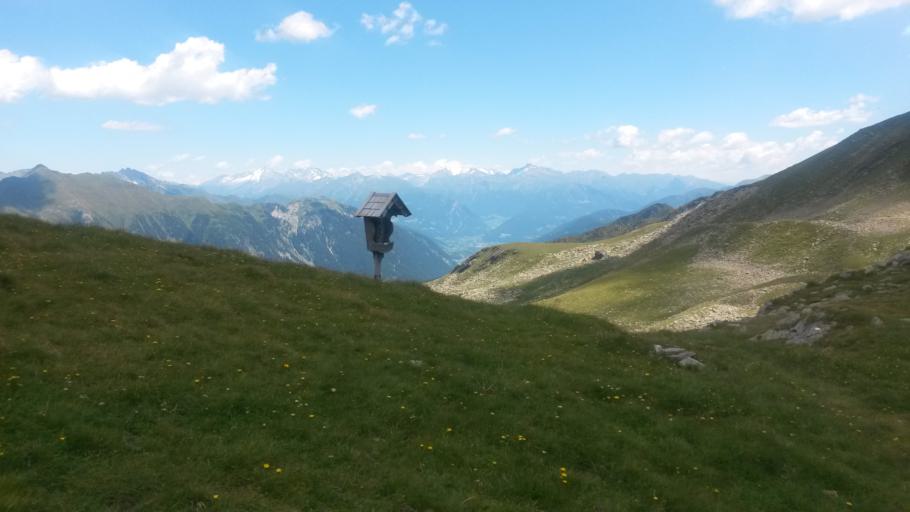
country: IT
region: Trentino-Alto Adige
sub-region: Bolzano
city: San Leonardo in Passiria
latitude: 46.8448
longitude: 11.2408
